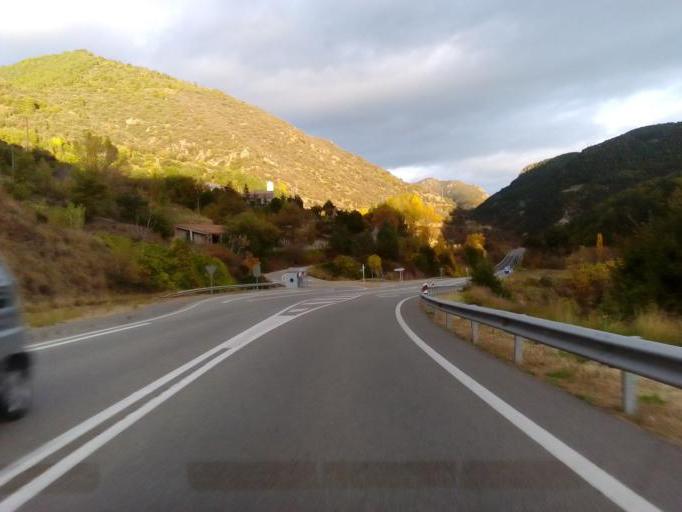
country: ES
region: Catalonia
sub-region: Provincia de Lleida
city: el Pont de Bar
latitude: 42.3713
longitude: 1.6007
